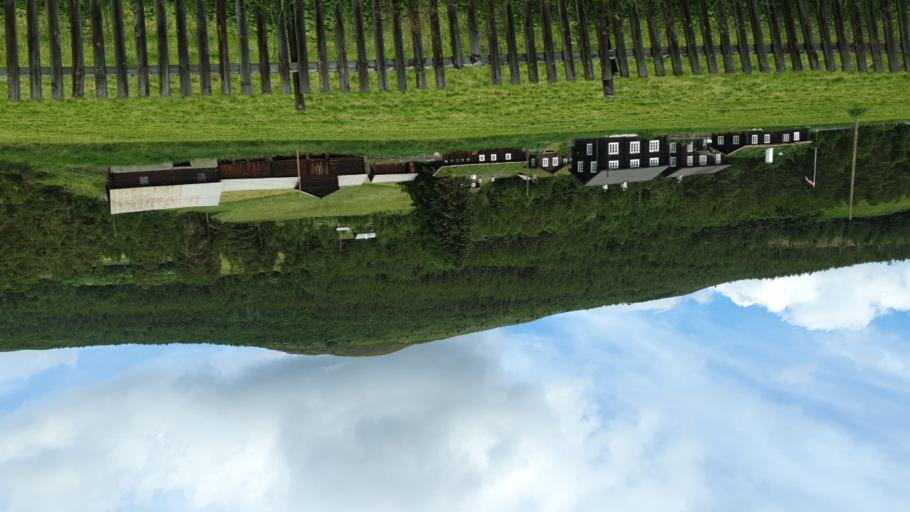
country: NO
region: Oppland
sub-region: Vaga
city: Vagamo
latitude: 61.7280
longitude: 9.0698
